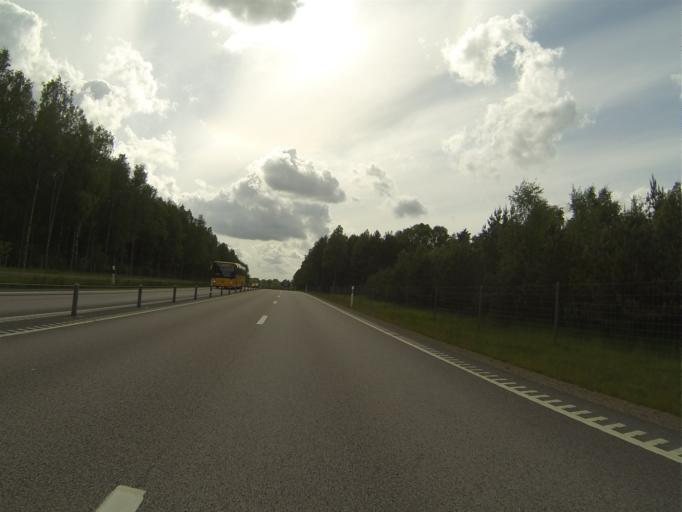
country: SE
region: Skane
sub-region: Sjobo Kommun
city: Blentarp
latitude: 55.6401
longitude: 13.5915
